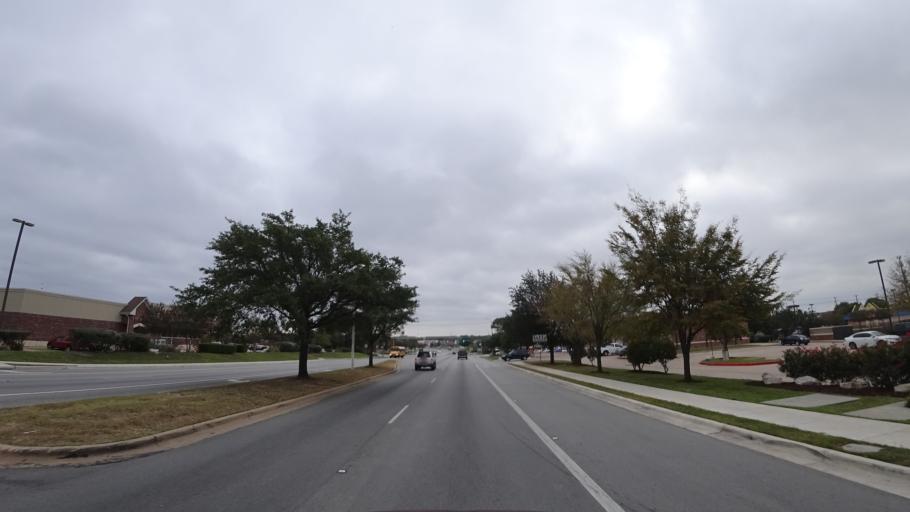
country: US
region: Texas
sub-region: Williamson County
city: Cedar Park
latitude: 30.4820
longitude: -97.8339
